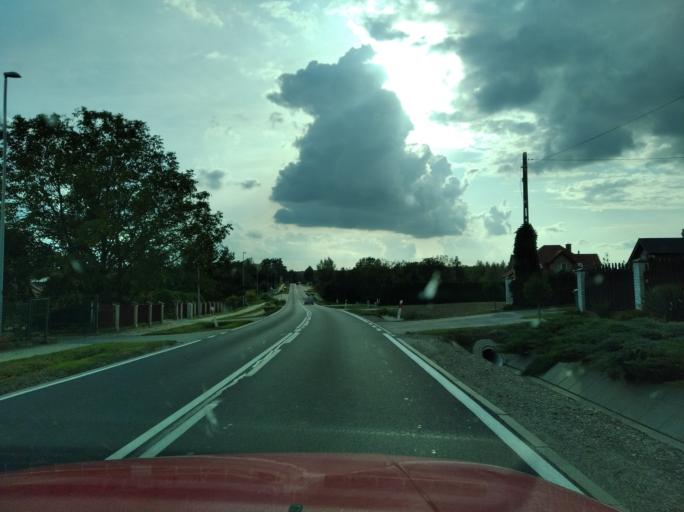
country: PL
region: Subcarpathian Voivodeship
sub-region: Powiat jaroslawski
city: Pawlosiow
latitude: 49.9856
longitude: 22.6545
